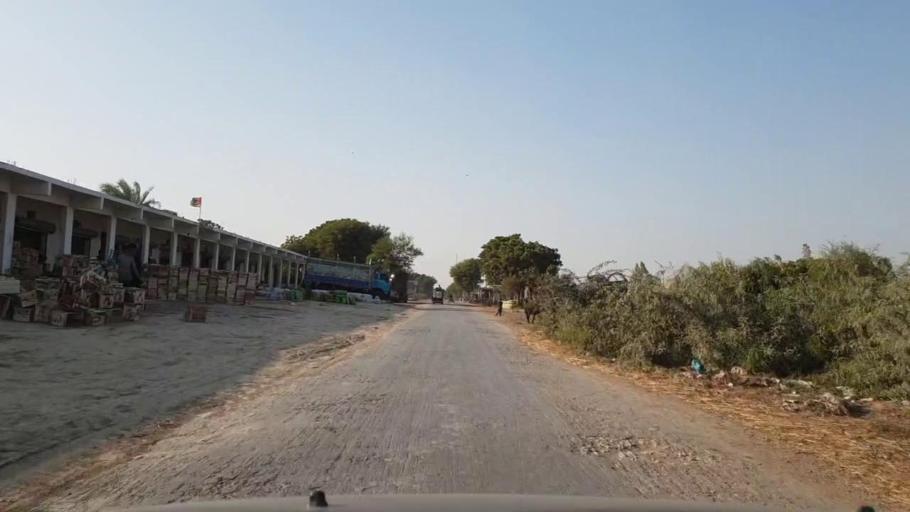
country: PK
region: Sindh
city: Chambar
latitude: 25.2073
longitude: 68.7857
